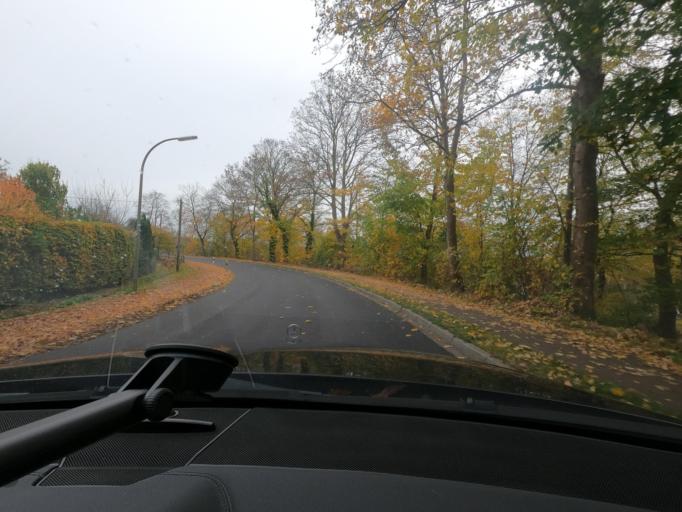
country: DE
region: North Rhine-Westphalia
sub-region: Regierungsbezirk Arnsberg
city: Mohnesee
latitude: 51.4873
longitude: 8.0951
